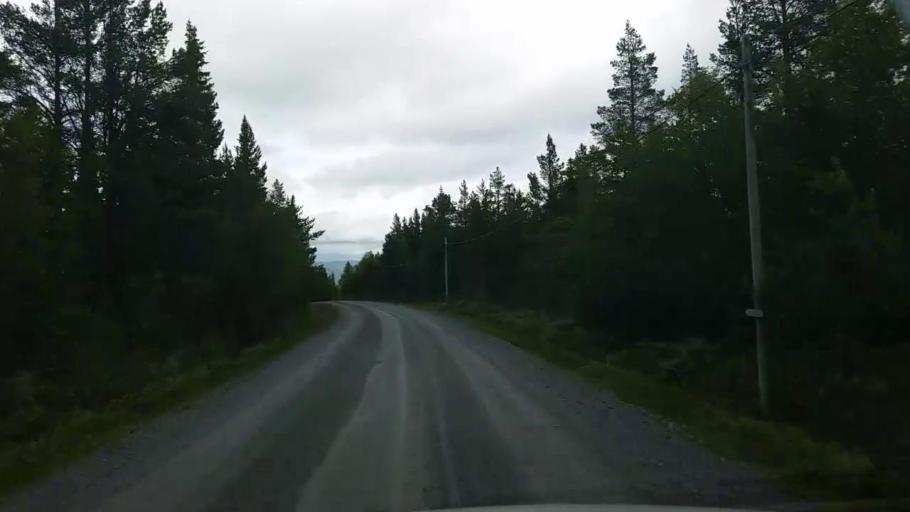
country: NO
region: Hedmark
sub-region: Engerdal
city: Engerdal
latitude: 62.4063
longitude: 12.6667
